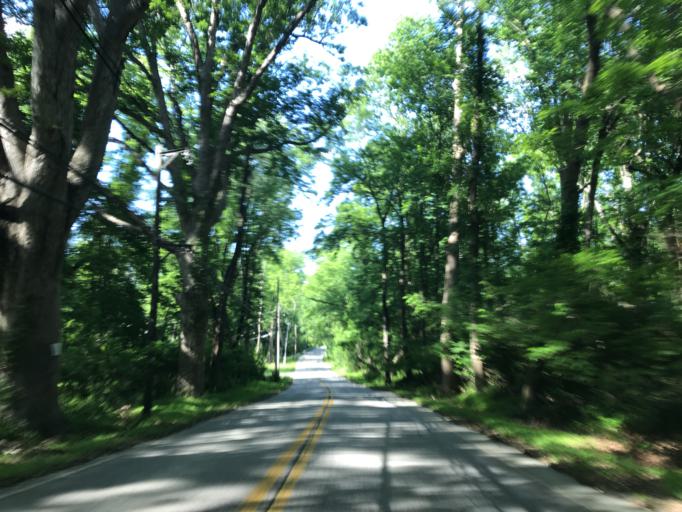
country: US
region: Maryland
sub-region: Baltimore County
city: Garrison
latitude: 39.4347
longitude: -76.7355
